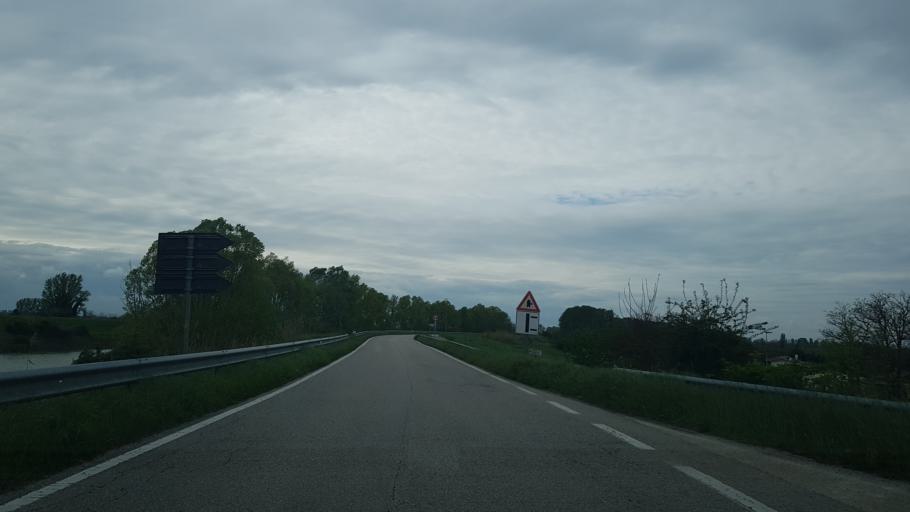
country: IT
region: Veneto
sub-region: Provincia di Padova
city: Barbona
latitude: 45.1023
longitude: 11.7058
